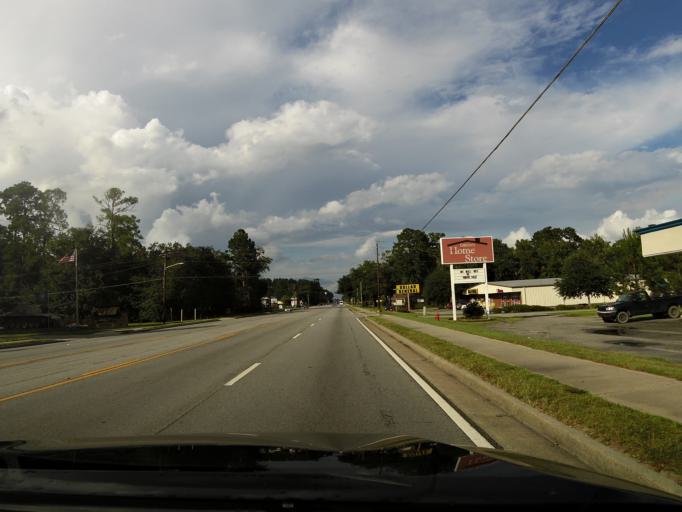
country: US
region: Georgia
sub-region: Liberty County
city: Hinesville
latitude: 31.8080
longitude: -81.6035
